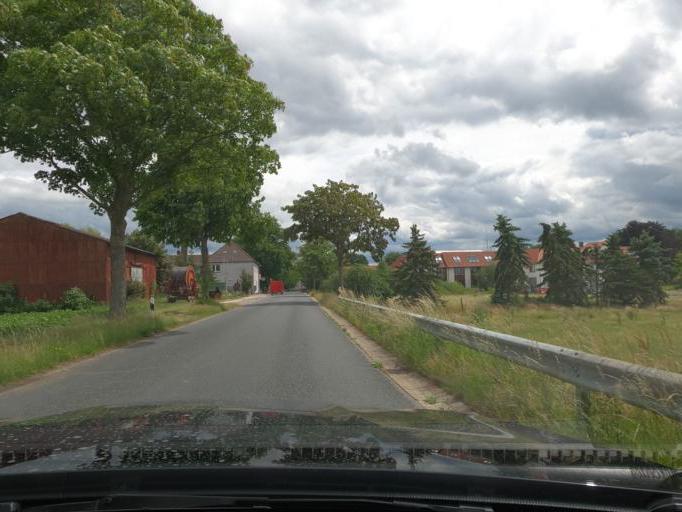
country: DE
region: Lower Saxony
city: Burgdorf
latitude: 52.4168
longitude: 9.9753
